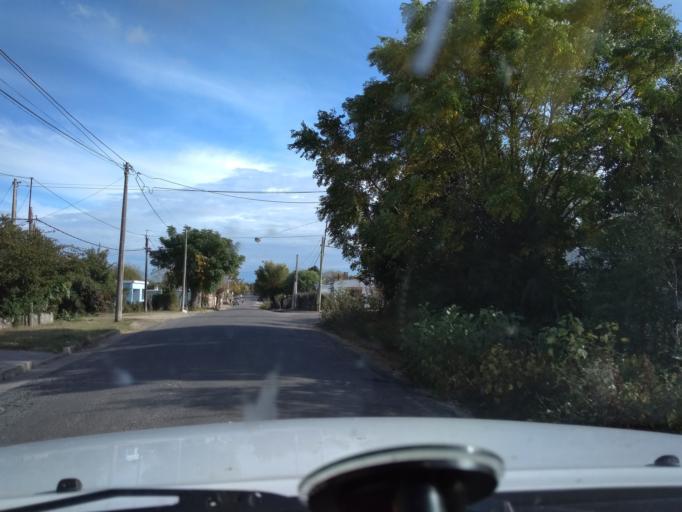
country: UY
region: Florida
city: Florida
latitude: -34.1063
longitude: -56.2180
